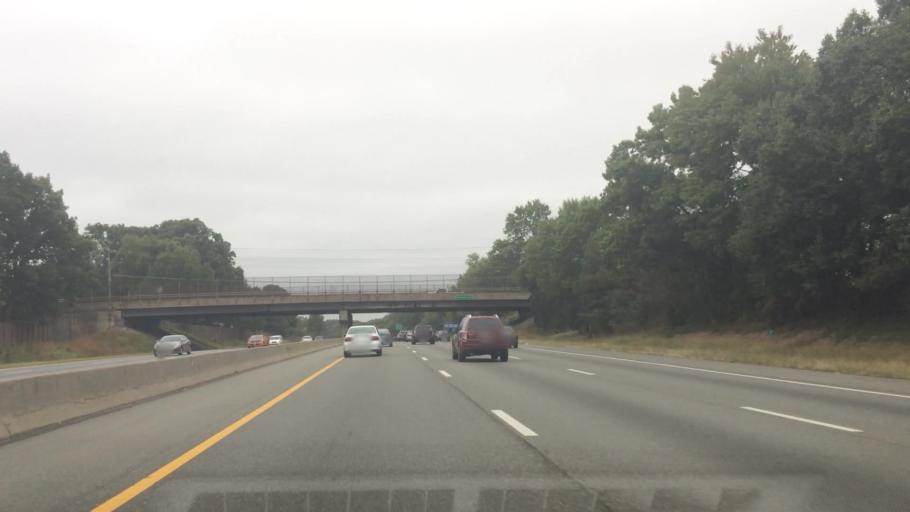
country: US
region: Virginia
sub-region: City of Colonial Heights
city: Colonial Heights
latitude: 37.2661
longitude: -77.3965
